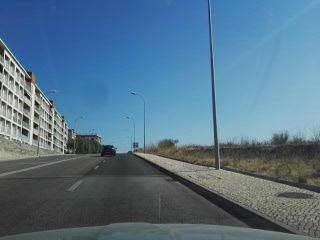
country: PT
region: Lisbon
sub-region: Oeiras
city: Alges
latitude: 38.7193
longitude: -9.2222
